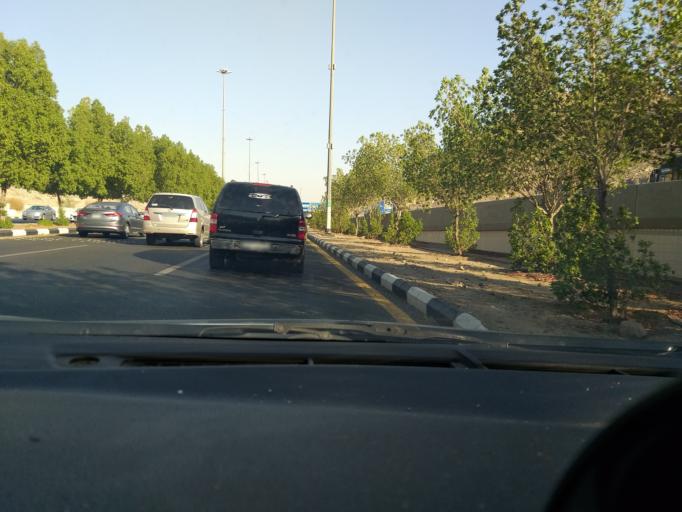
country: SA
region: Makkah
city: Mecca
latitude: 21.3937
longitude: 39.8542
